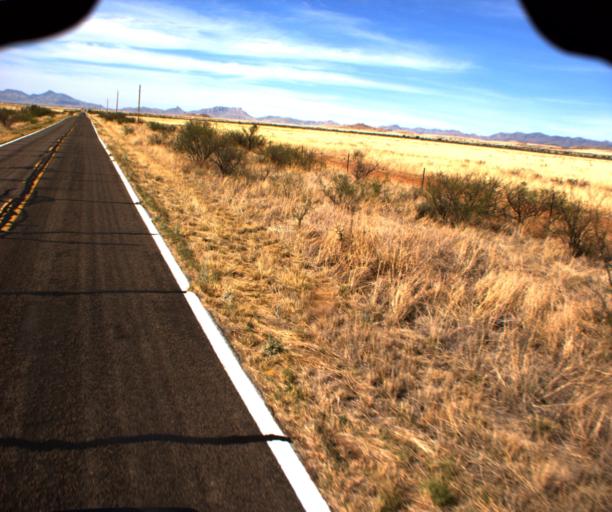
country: US
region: Arizona
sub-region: Cochise County
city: Willcox
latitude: 31.9019
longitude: -109.4914
